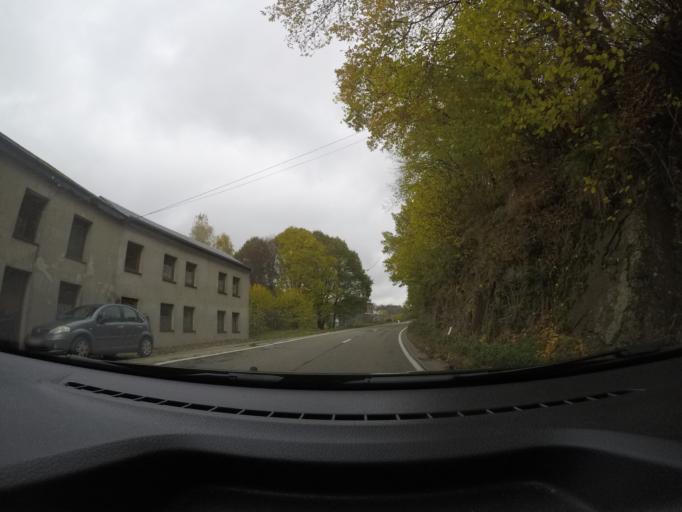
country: BE
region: Wallonia
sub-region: Province du Luxembourg
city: Houffalize
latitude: 50.0971
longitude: 5.7428
